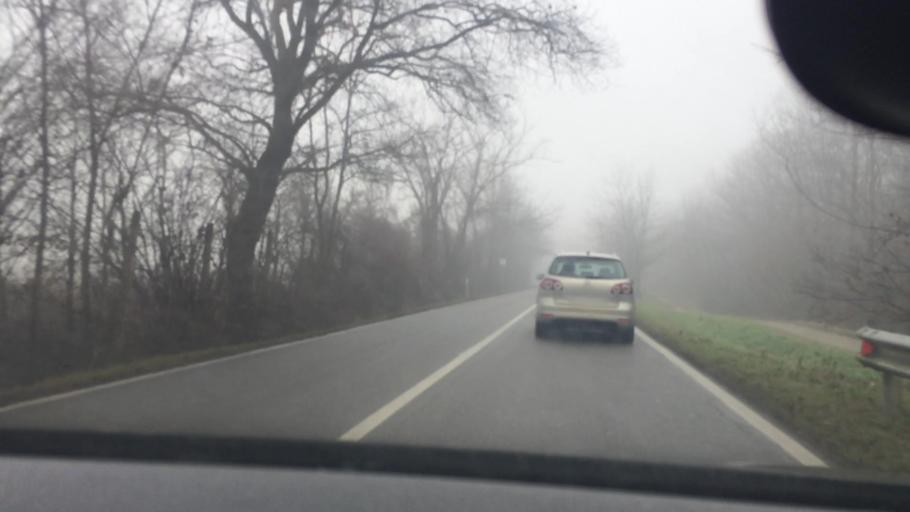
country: IT
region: Lombardy
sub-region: Provincia di Monza e Brianza
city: Ceriano Laghetto
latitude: 45.6296
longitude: 9.0964
